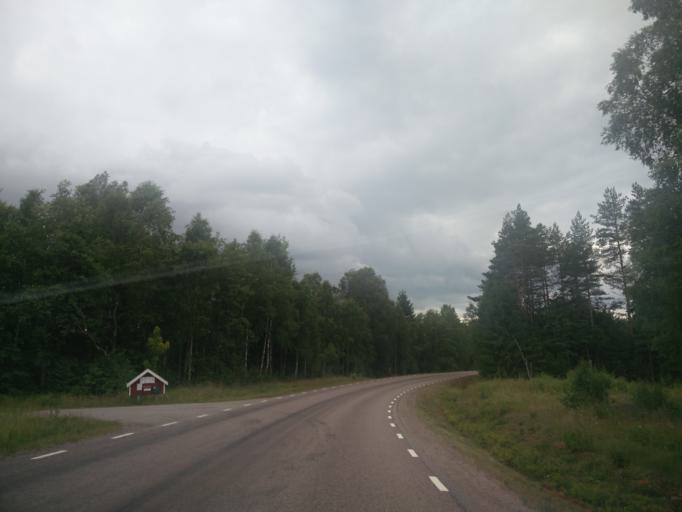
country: SE
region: Vaermland
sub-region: Arvika Kommun
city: Arvika
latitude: 59.9435
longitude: 12.6892
